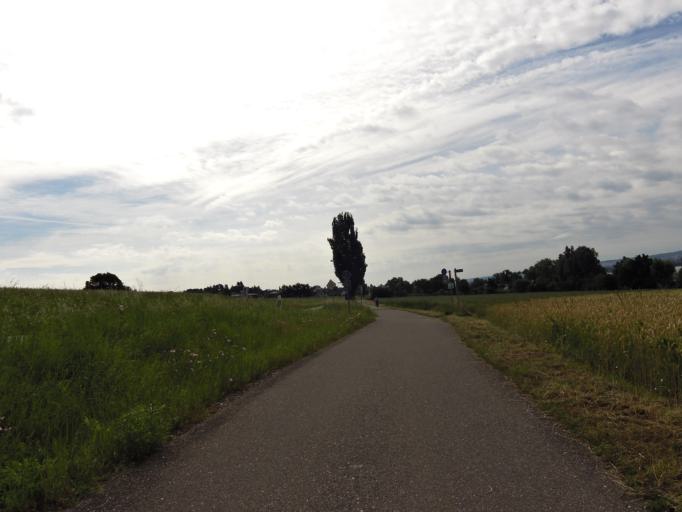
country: DE
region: Baden-Wuerttemberg
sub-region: Freiburg Region
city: Allensbach
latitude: 47.7240
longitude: 9.0457
